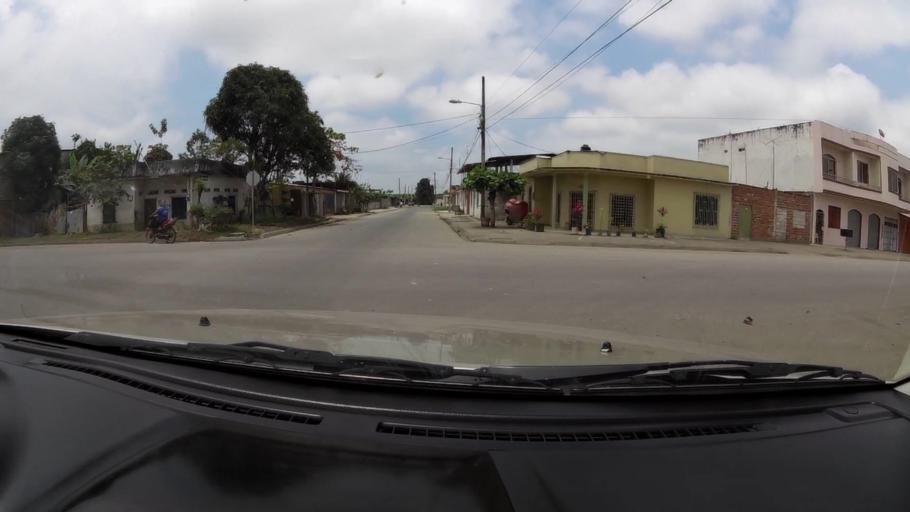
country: EC
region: El Oro
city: Pasaje
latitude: -3.2378
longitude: -79.8272
